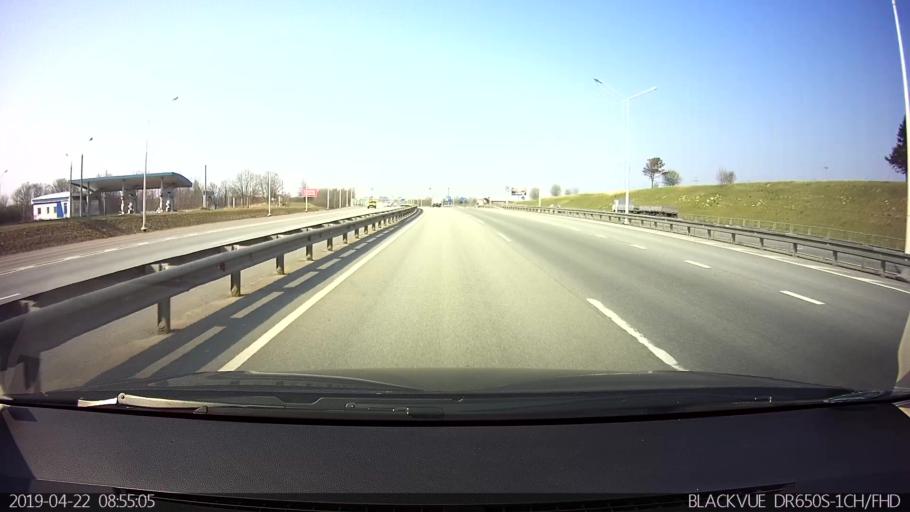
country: RU
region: Smolensk
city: Pechersk
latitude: 54.8838
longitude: 32.0756
